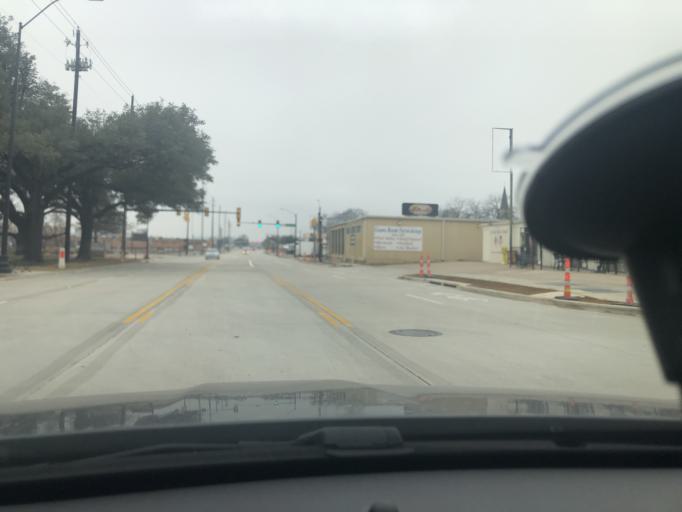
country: US
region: Texas
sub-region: Tarrant County
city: Westworth
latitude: 32.7370
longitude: -97.3700
